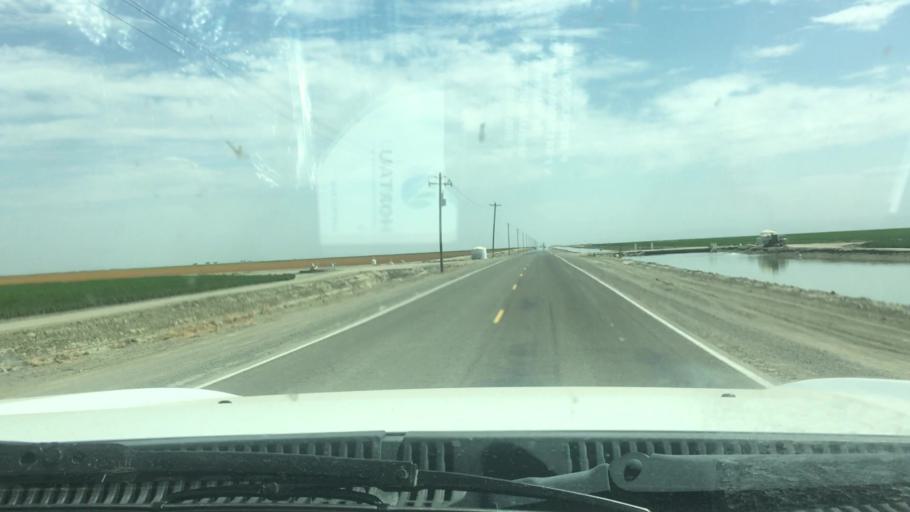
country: US
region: California
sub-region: Tulare County
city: Alpaugh
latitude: 35.9073
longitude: -119.5734
